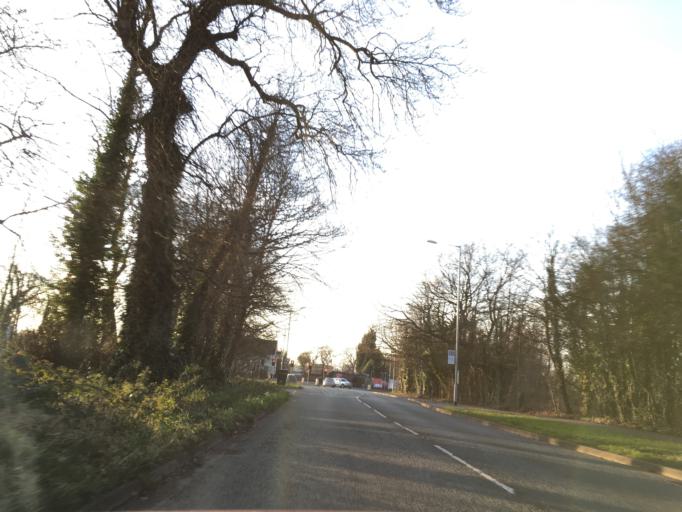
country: GB
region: England
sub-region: Borough of Stockport
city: Cheadle Hulme
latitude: 53.3588
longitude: -2.2176
